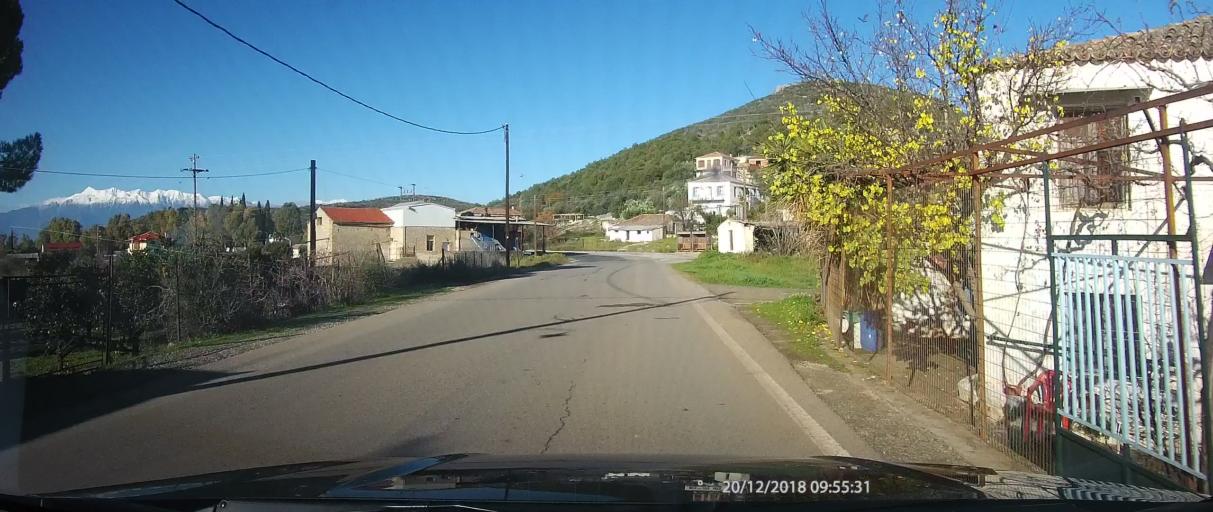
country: GR
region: Peloponnese
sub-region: Nomos Lakonias
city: Yerakion
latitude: 37.0248
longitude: 22.6219
